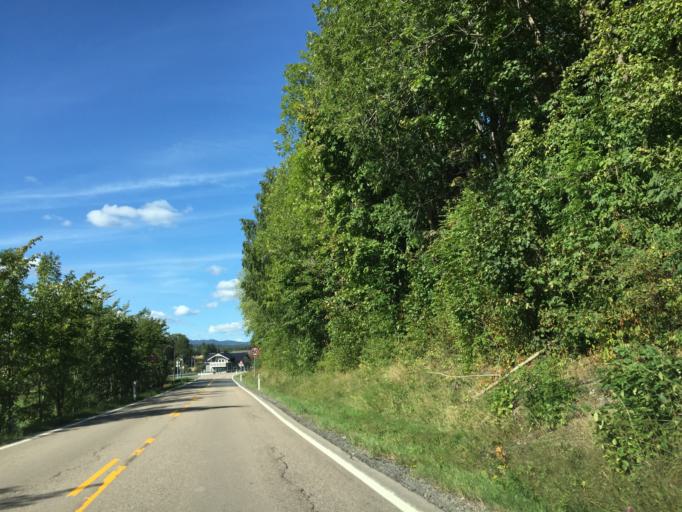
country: NO
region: Buskerud
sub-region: Ovre Eiker
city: Hokksund
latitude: 59.7052
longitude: 9.8639
